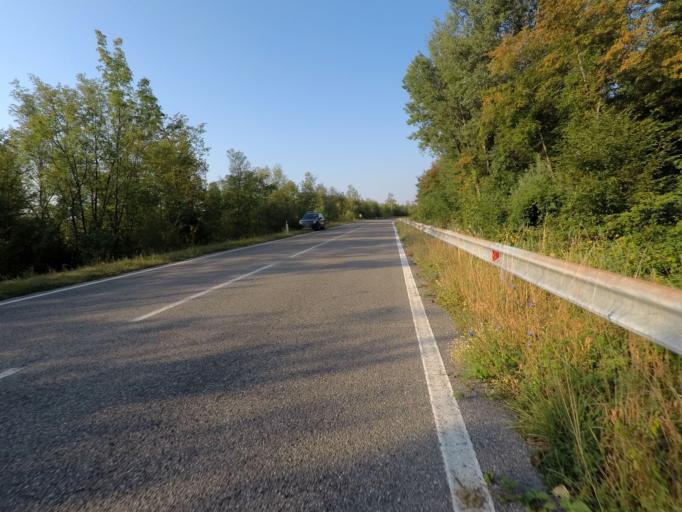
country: IT
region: Friuli Venezia Giulia
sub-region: Provincia di Udine
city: Trasaghis
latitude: 46.2705
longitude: 13.0558
